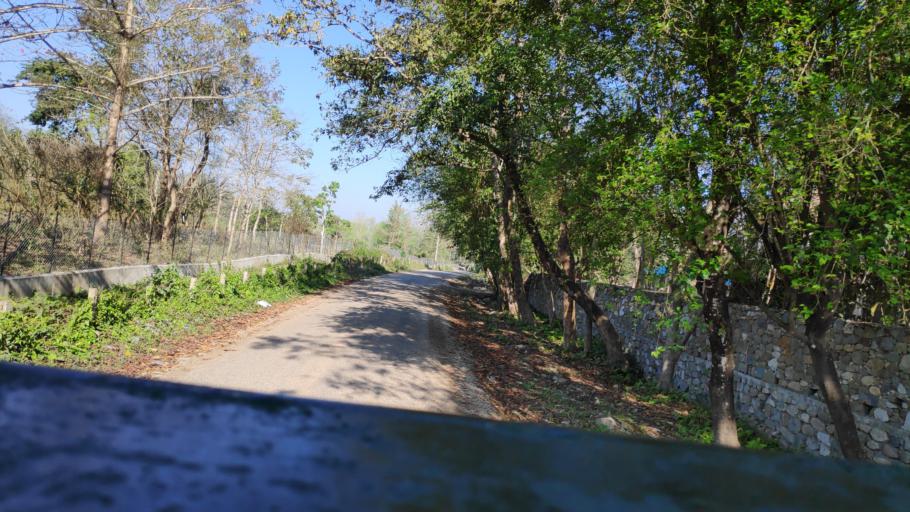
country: NP
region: Central Region
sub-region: Narayani Zone
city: Bharatpur
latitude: 27.5678
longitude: 84.5202
